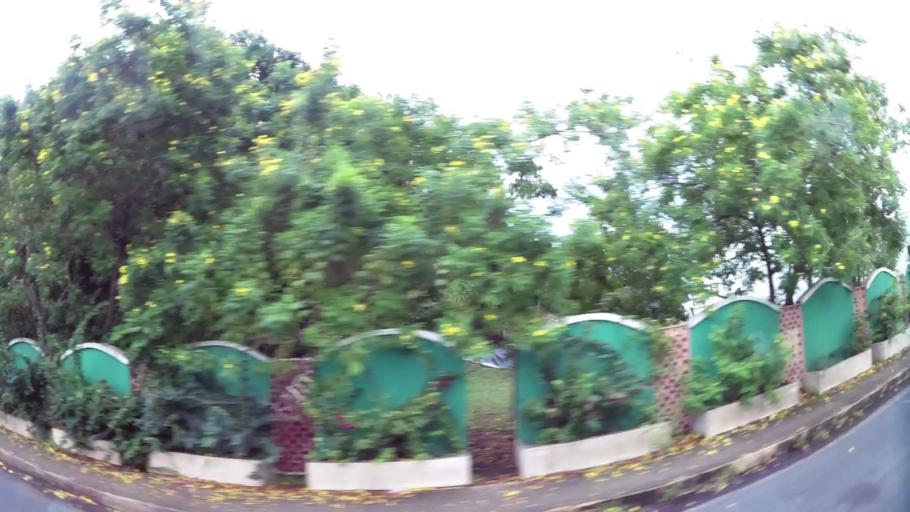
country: PA
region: Panama
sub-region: Distrito de Panama
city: Ancon
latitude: 8.9127
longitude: -79.5249
